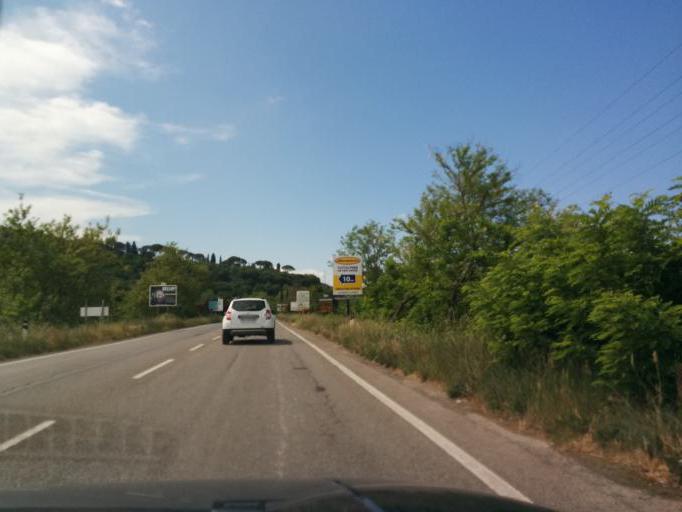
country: IT
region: Tuscany
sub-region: Provincia di Siena
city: Poggibonsi
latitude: 43.4769
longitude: 11.1300
